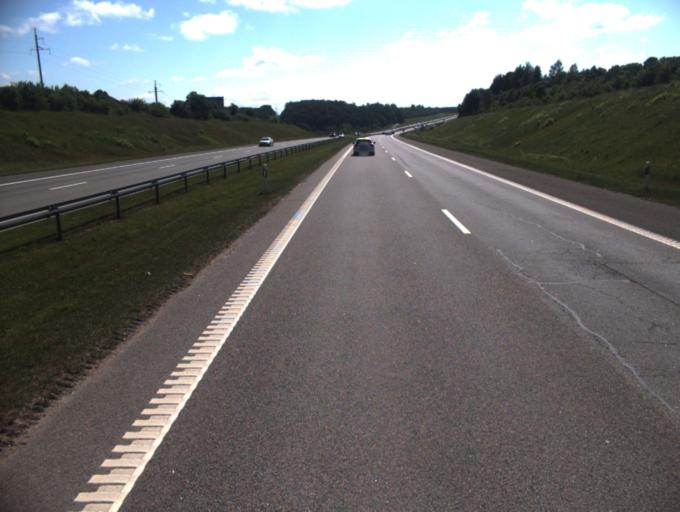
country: LT
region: Klaipedos apskritis
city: Gargzdai
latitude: 55.7307
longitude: 21.4017
